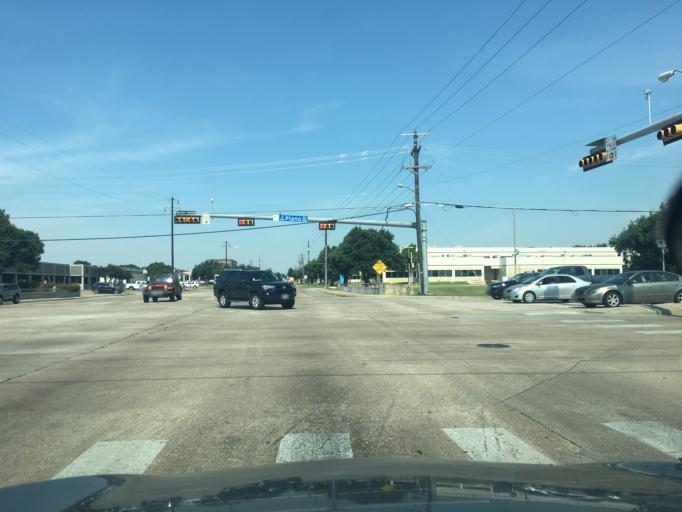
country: US
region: Texas
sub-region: Dallas County
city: Richardson
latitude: 32.9607
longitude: -96.6996
